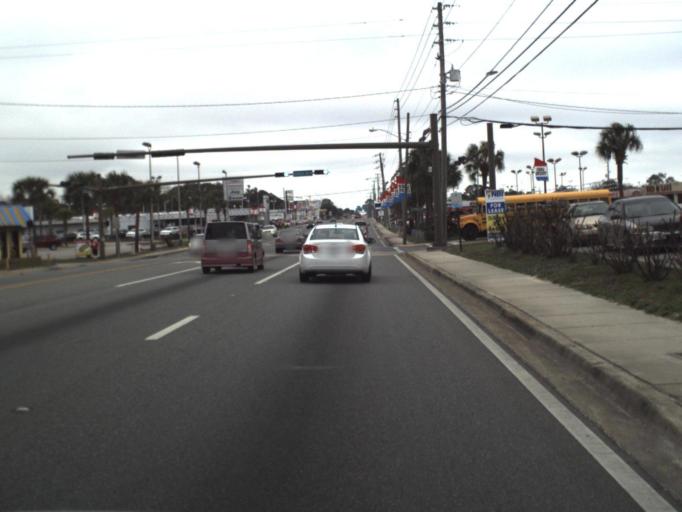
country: US
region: Florida
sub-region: Bay County
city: Panama City
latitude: 30.1751
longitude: -85.6700
